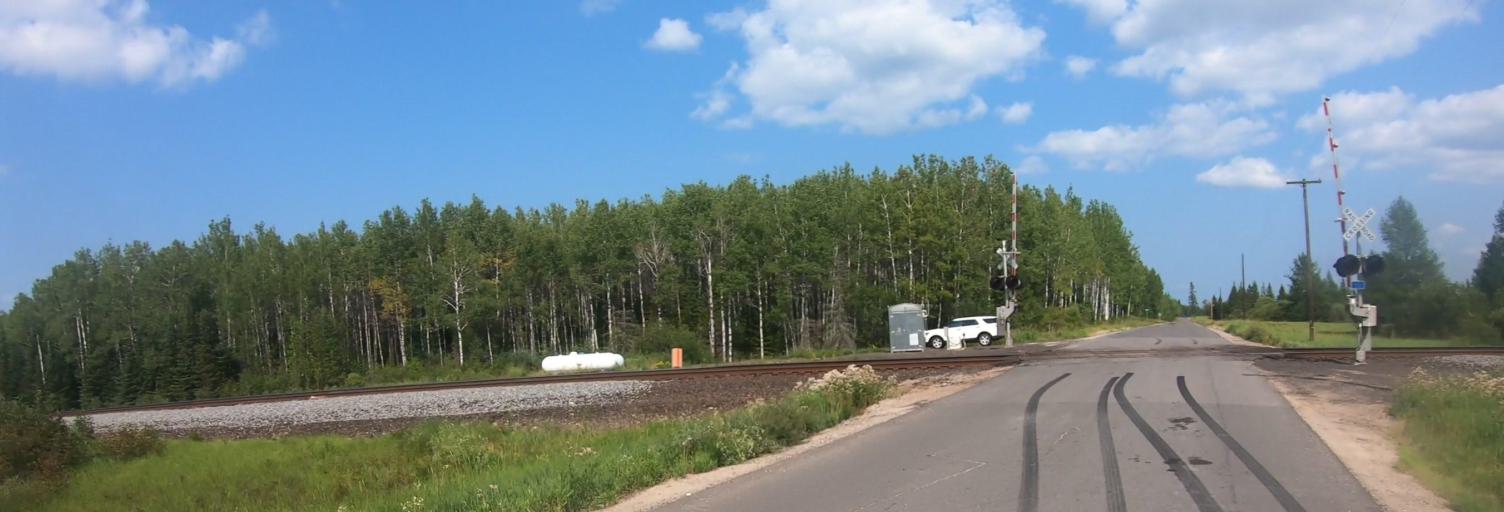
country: US
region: Minnesota
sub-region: Saint Louis County
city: Mountain Iron
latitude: 47.8920
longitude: -92.7139
